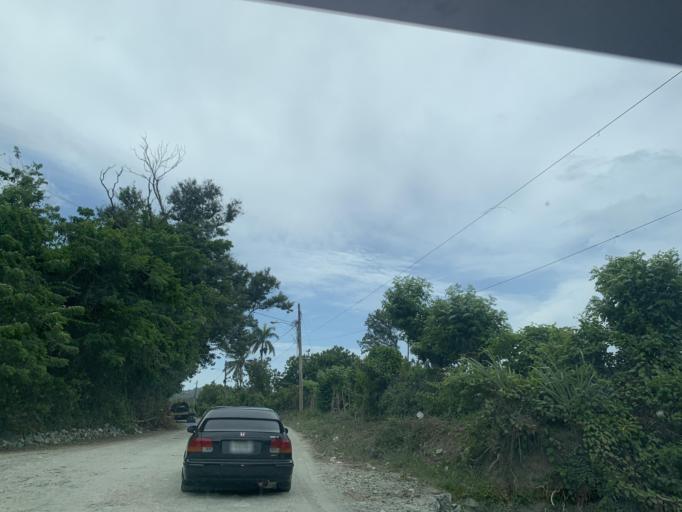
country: DO
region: Puerto Plata
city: Imbert
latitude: 19.8198
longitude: -70.7801
